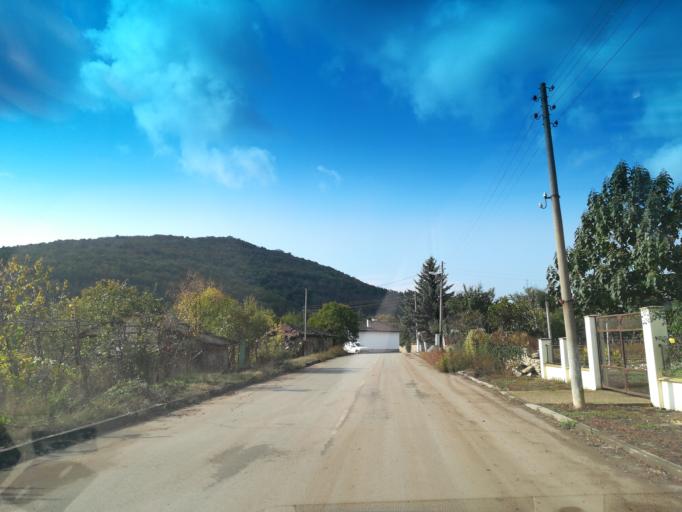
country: BG
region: Stara Zagora
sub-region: Obshtina Nikolaevo
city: Elkhovo
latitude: 42.3409
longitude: 25.4043
